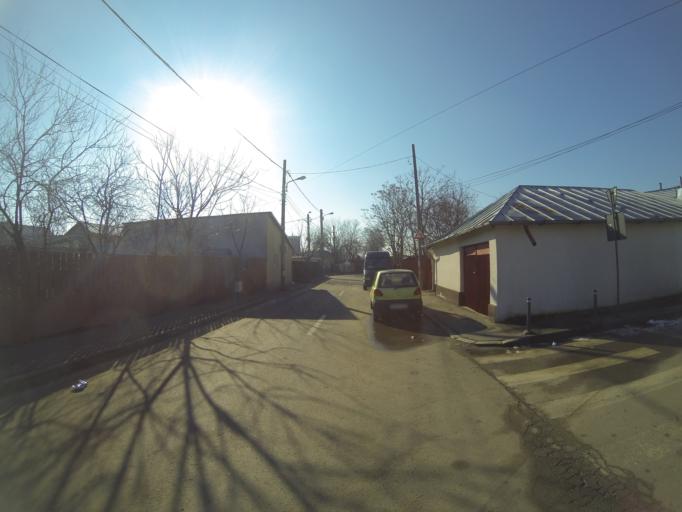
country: RO
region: Ilfov
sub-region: Comuna Magurele
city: Magurele
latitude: 44.3909
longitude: 26.0569
